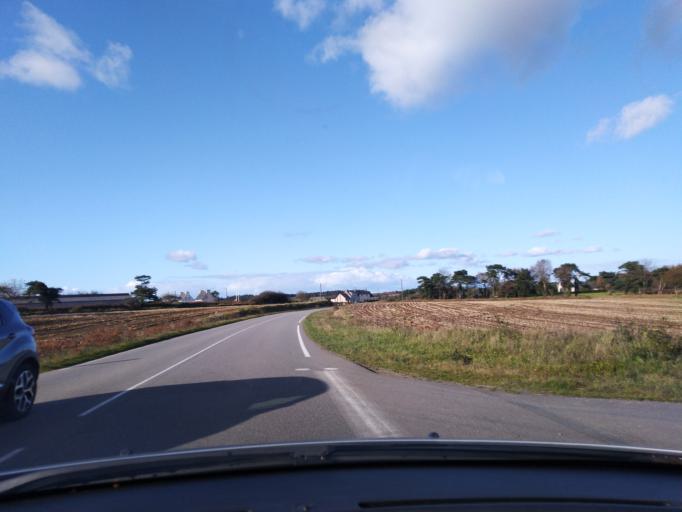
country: FR
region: Brittany
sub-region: Departement du Finistere
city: Guerlesquin
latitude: 48.5287
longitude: -3.5978
